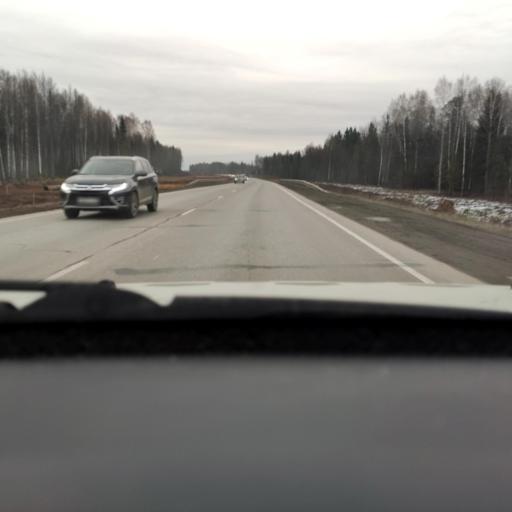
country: RU
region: Perm
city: Polazna
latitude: 58.1338
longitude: 56.4212
